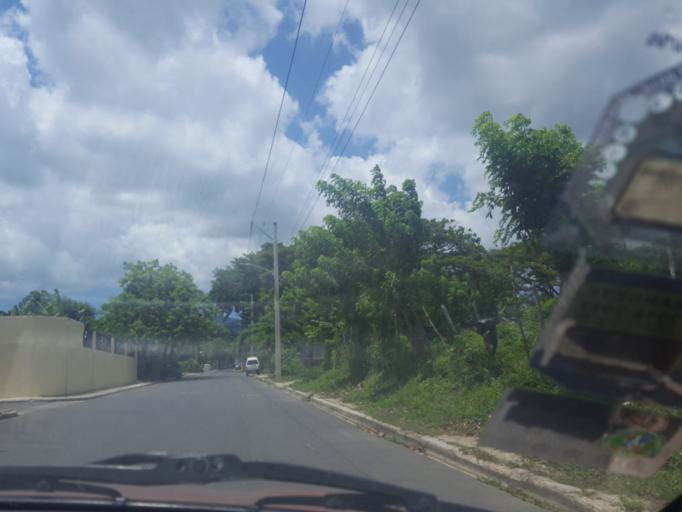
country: DO
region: Santiago
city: Santiago de los Caballeros
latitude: 19.4796
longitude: -70.6588
